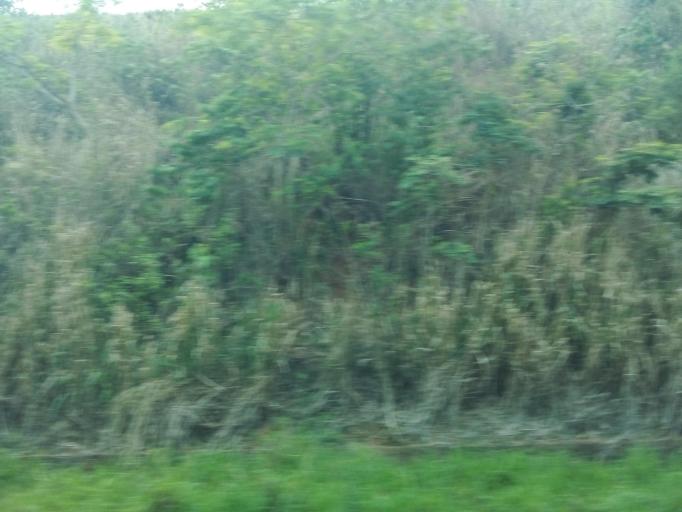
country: BR
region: Minas Gerais
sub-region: Governador Valadares
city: Governador Valadares
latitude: -19.0964
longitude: -42.1652
